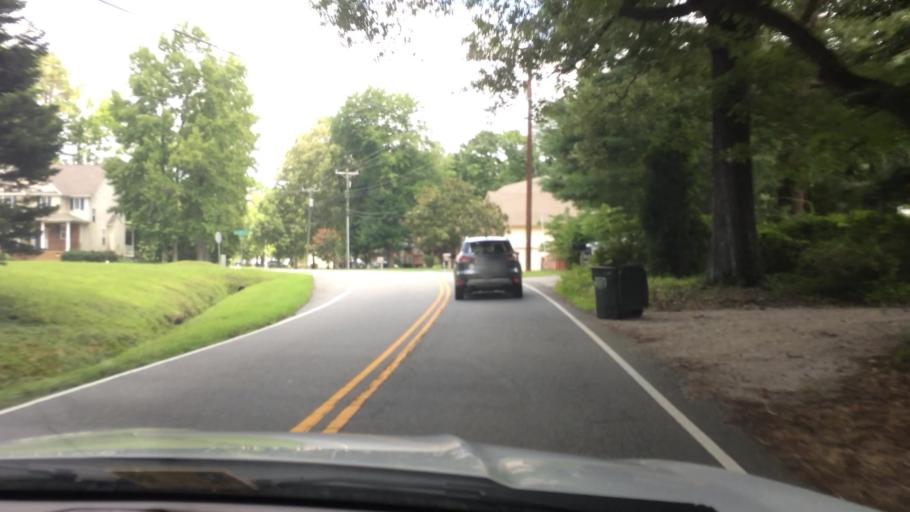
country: US
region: Virginia
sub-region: City of Poquoson
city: Poquoson
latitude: 37.1476
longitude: -76.4481
